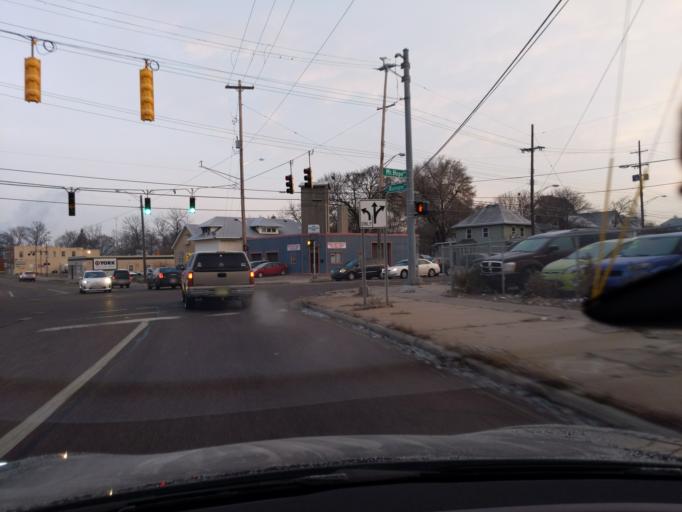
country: US
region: Michigan
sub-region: Ingham County
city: Lansing
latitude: 42.7117
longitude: -84.5526
